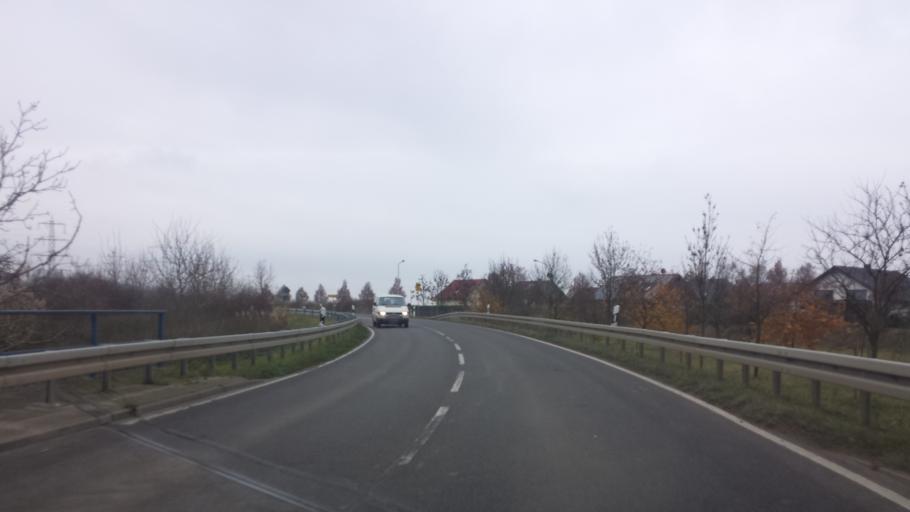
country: DE
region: Rheinland-Pfalz
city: Worms
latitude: 49.6572
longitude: 8.3981
